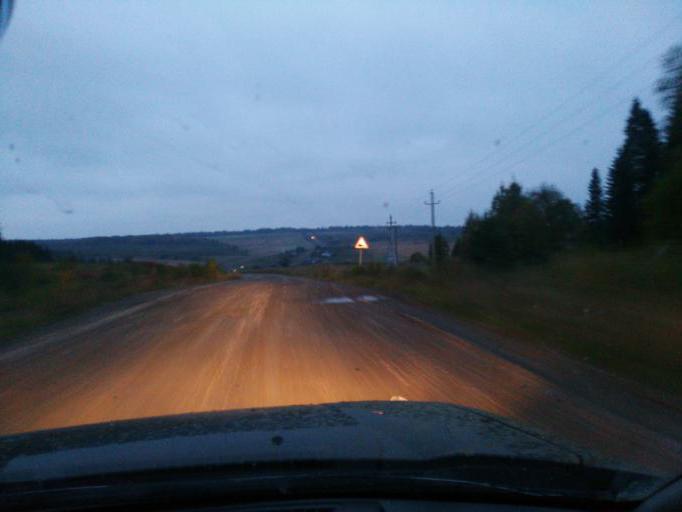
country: RU
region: Perm
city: Gornozavodsk
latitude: 57.9043
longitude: 58.3711
